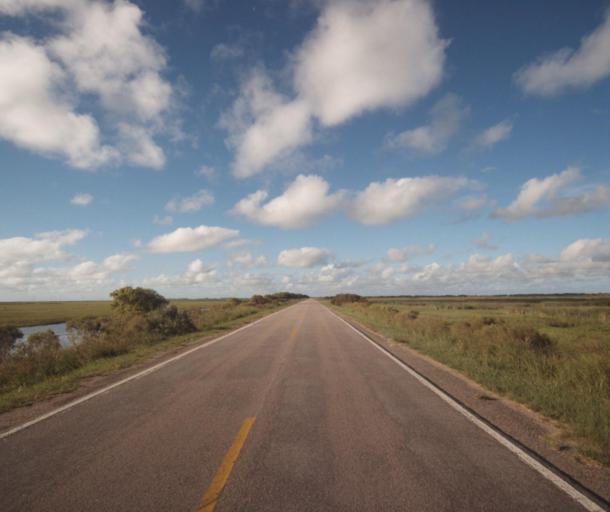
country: BR
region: Rio Grande do Sul
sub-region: Arroio Grande
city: Arroio Grande
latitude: -32.6042
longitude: -52.5707
